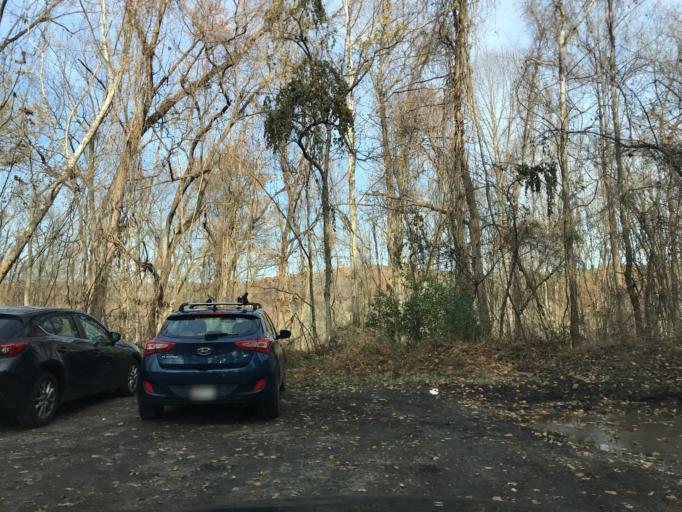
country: US
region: Maryland
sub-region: Carroll County
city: Eldersburg
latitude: 39.4419
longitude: -76.9024
